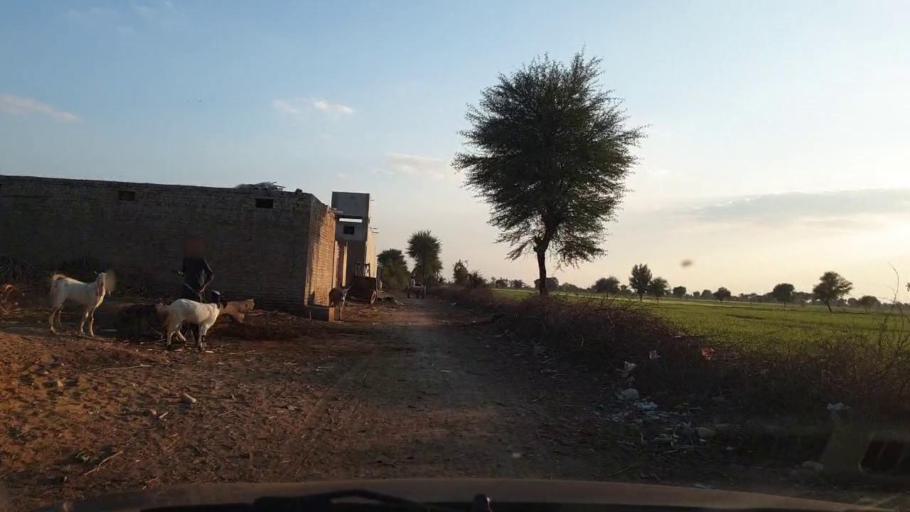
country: PK
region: Sindh
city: Sinjhoro
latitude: 25.9957
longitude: 68.8014
